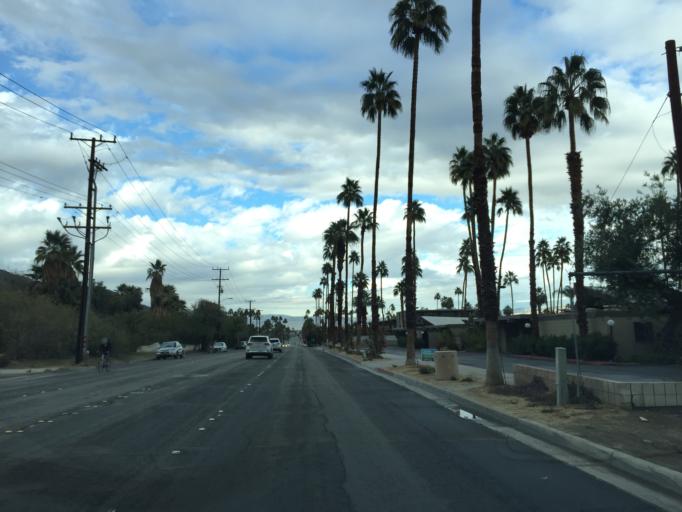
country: US
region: California
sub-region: Riverside County
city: Palm Springs
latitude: 33.7990
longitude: -116.5455
